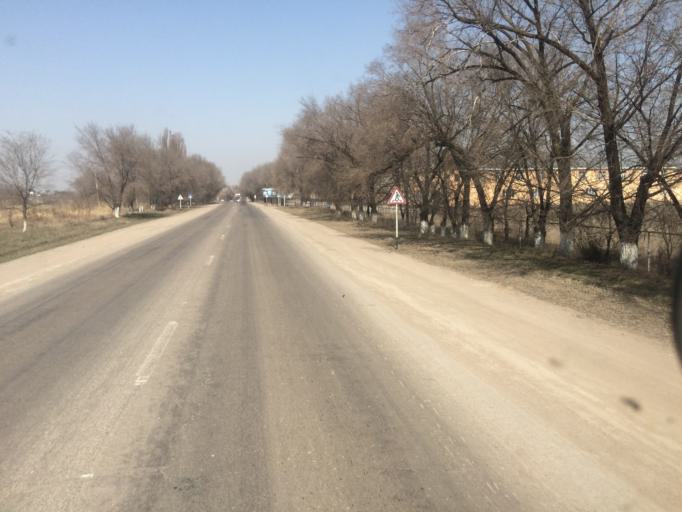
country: KZ
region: Almaty Oblysy
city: Burunday
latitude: 43.2982
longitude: 76.6729
